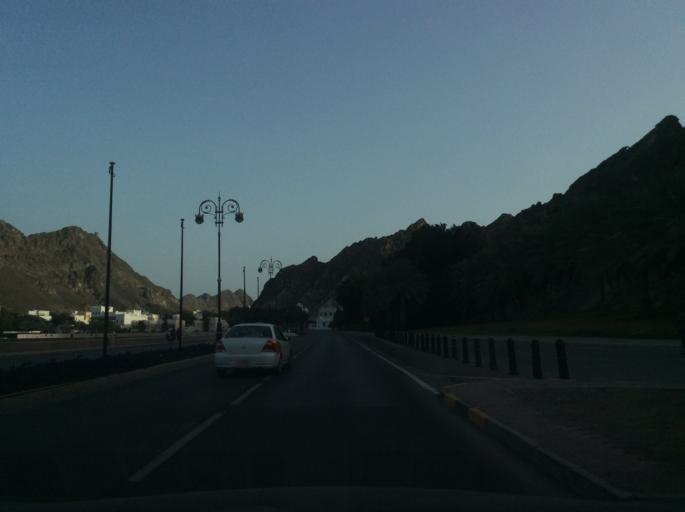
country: OM
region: Muhafazat Masqat
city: Muscat
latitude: 23.6233
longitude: 58.5812
